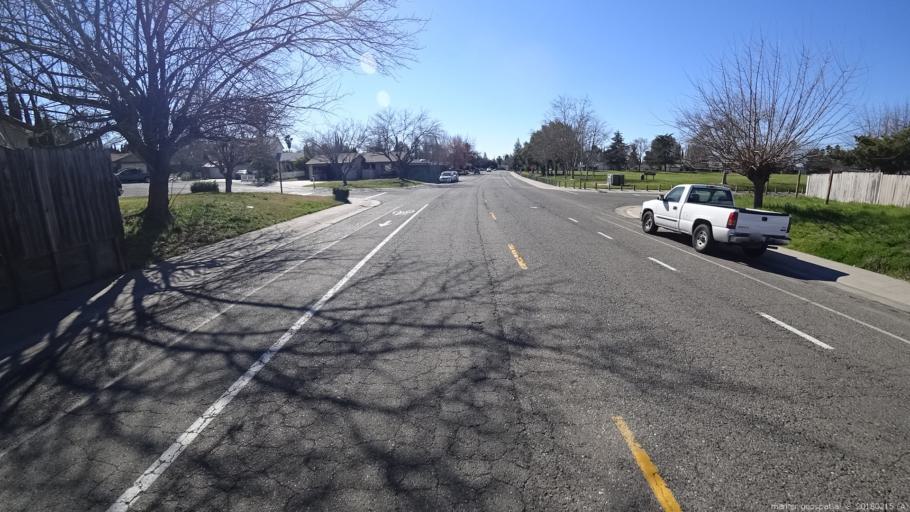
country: US
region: California
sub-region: Sacramento County
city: Antelope
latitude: 38.6945
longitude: -121.3327
